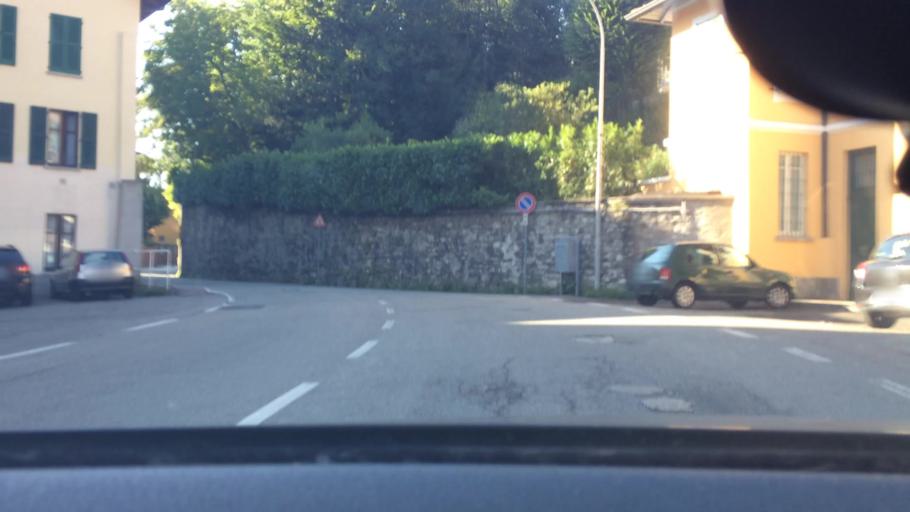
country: IT
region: Lombardy
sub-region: Provincia di Como
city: Brunate
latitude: 45.8091
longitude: 9.0944
